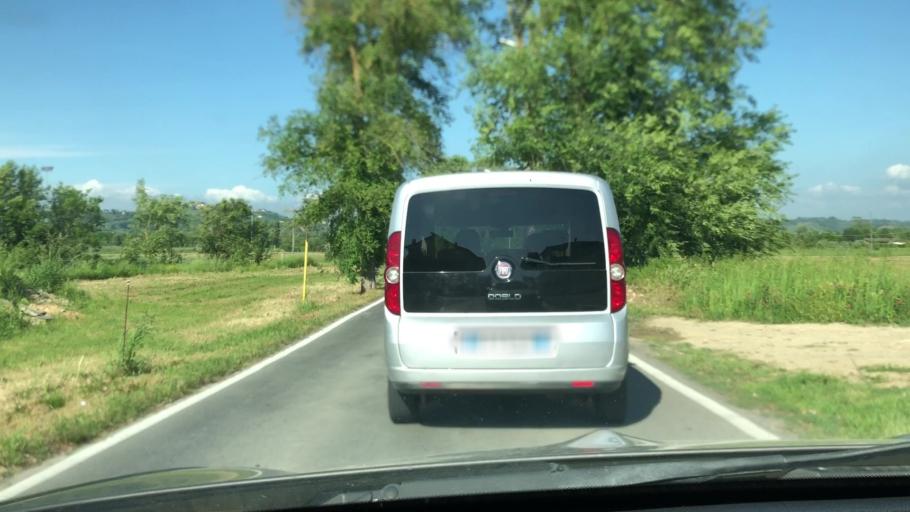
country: IT
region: Tuscany
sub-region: Province of Pisa
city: Capannoli
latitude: 43.5878
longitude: 10.6764
